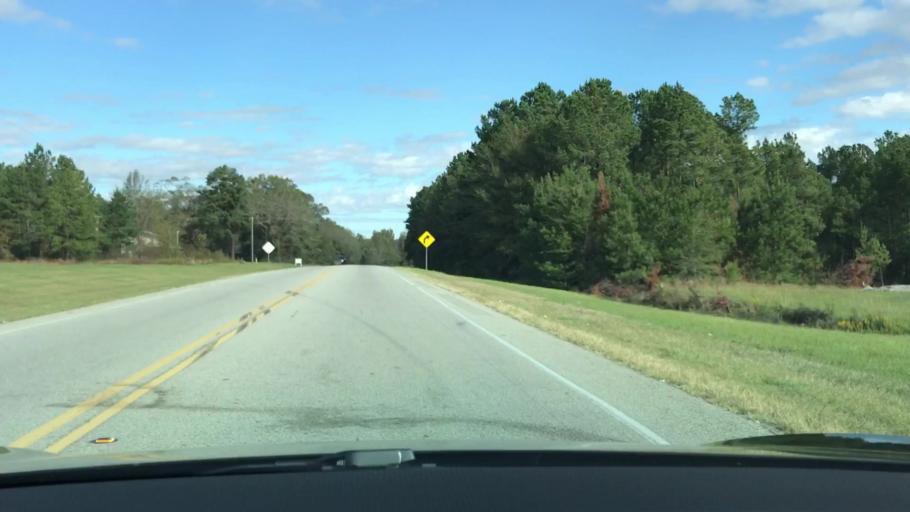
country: US
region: Georgia
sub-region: Jefferson County
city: Louisville
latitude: 32.9488
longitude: -82.3947
